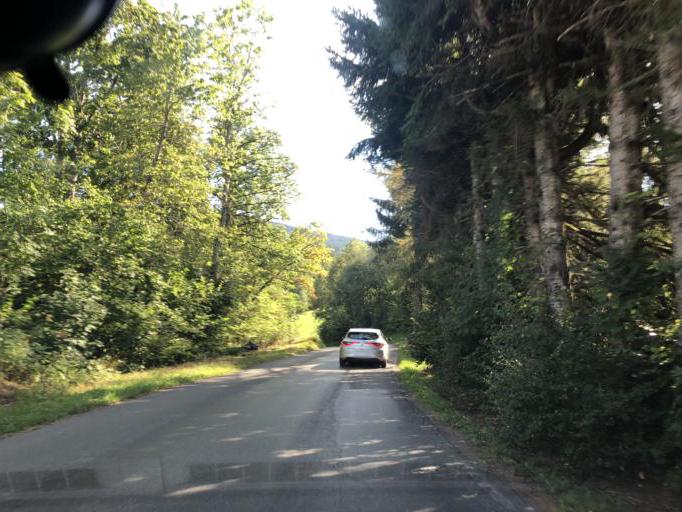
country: FR
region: Rhone-Alpes
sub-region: Departement de la Haute-Savoie
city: Cordon
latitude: 45.9153
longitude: 6.6081
